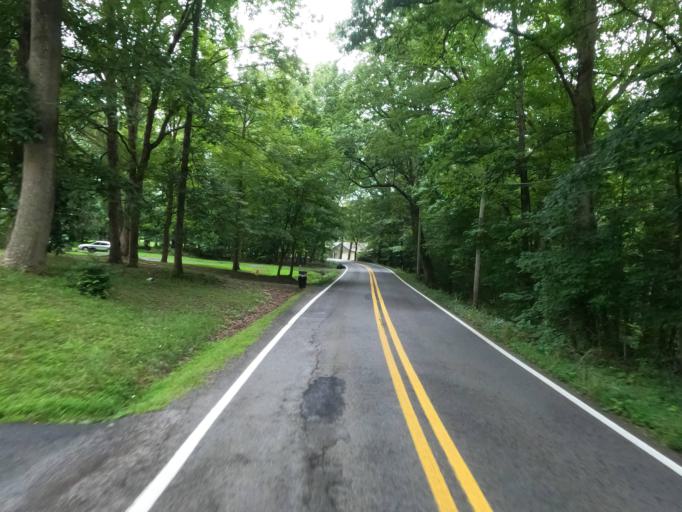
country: US
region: West Virginia
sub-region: Marion County
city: Fairmont
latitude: 39.5059
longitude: -80.1032
